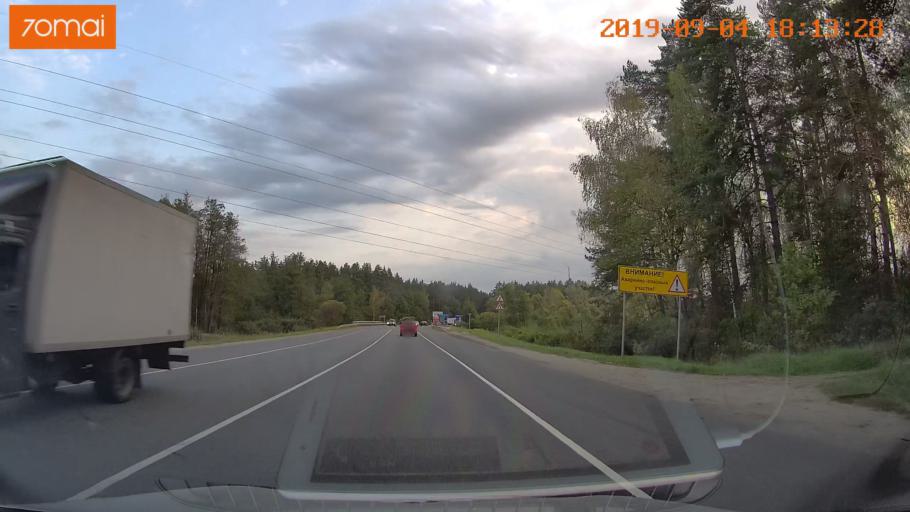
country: RU
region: Moskovskaya
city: Lopatinskiy
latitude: 55.3598
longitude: 38.7344
